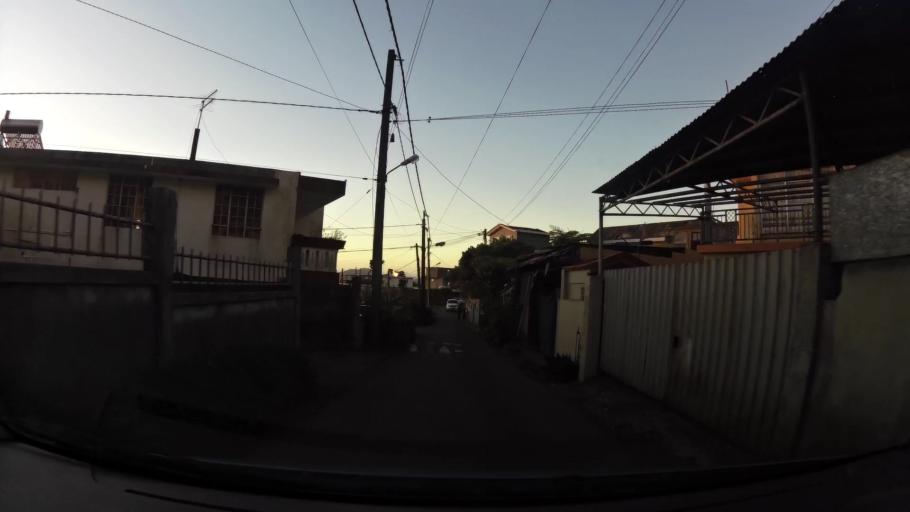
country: MU
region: Plaines Wilhems
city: Curepipe
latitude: -20.2994
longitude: 57.5234
